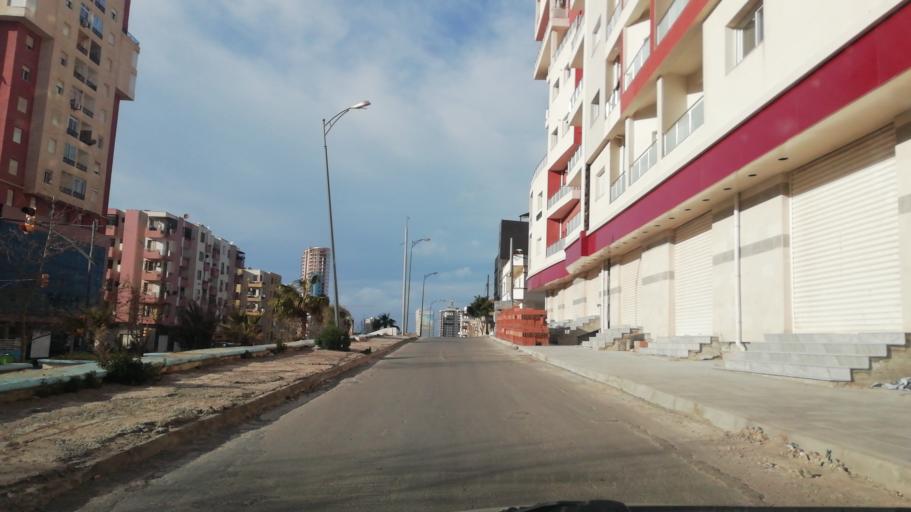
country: DZ
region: Oran
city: Bir el Djir
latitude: 35.7229
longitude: -0.5838
